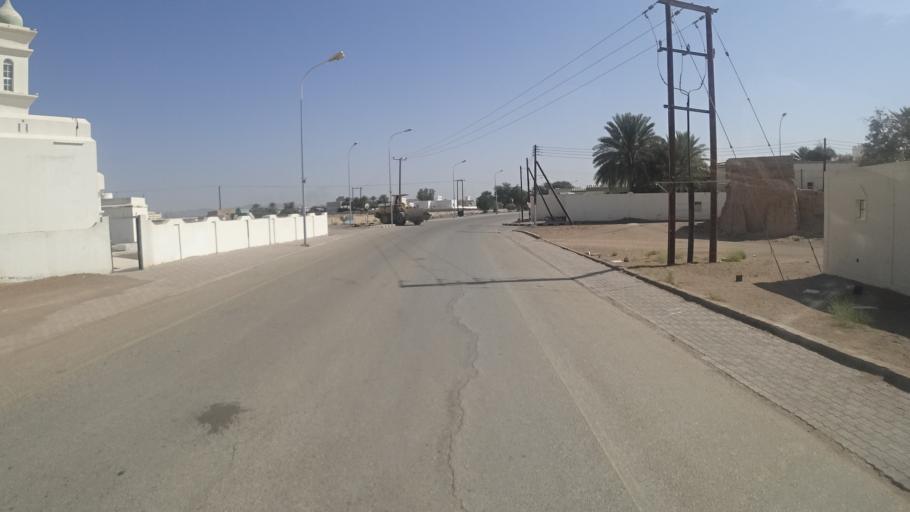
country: OM
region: Ash Sharqiyah
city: Badiyah
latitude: 22.5018
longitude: 58.7435
